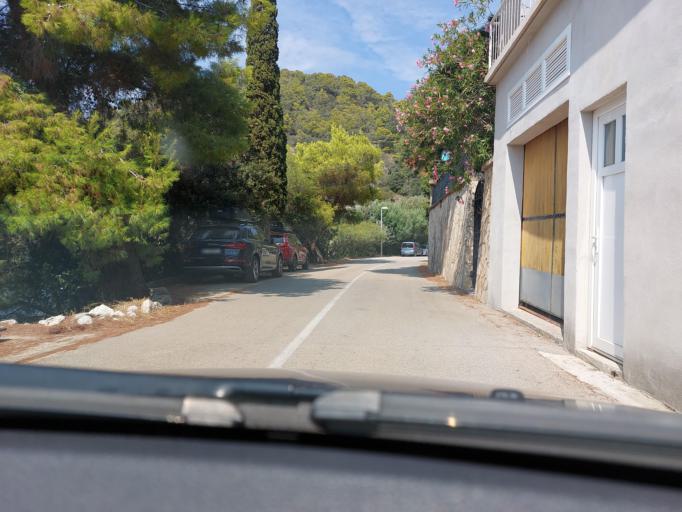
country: HR
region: Dubrovacko-Neretvanska
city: Smokvica
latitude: 42.7490
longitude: 16.8267
